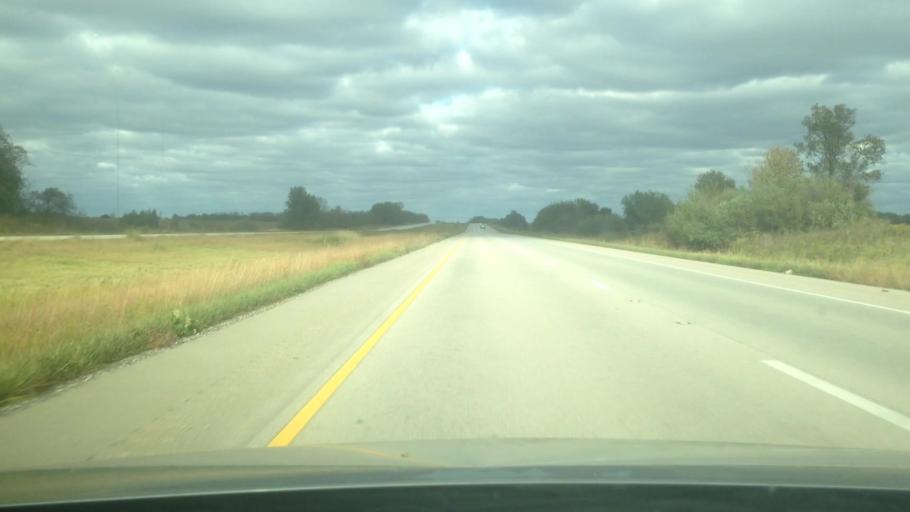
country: US
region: Illinois
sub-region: Macon County
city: Forsyth
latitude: 39.9216
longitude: -88.8564
